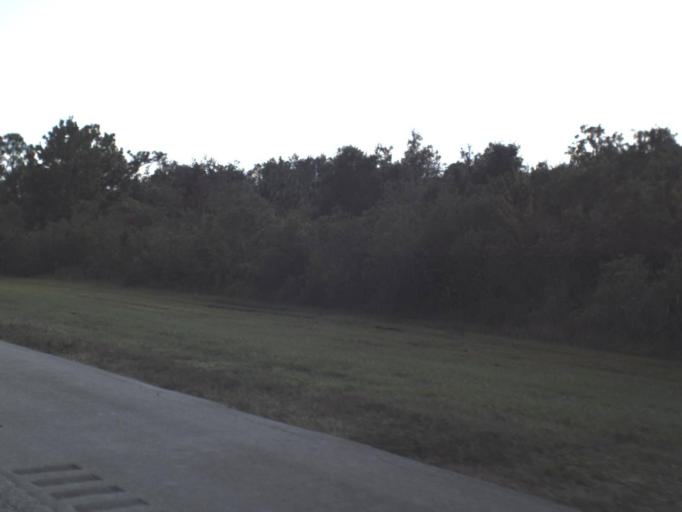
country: US
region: Florida
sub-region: Indian River County
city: Fellsmere
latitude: 27.7362
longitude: -80.9225
